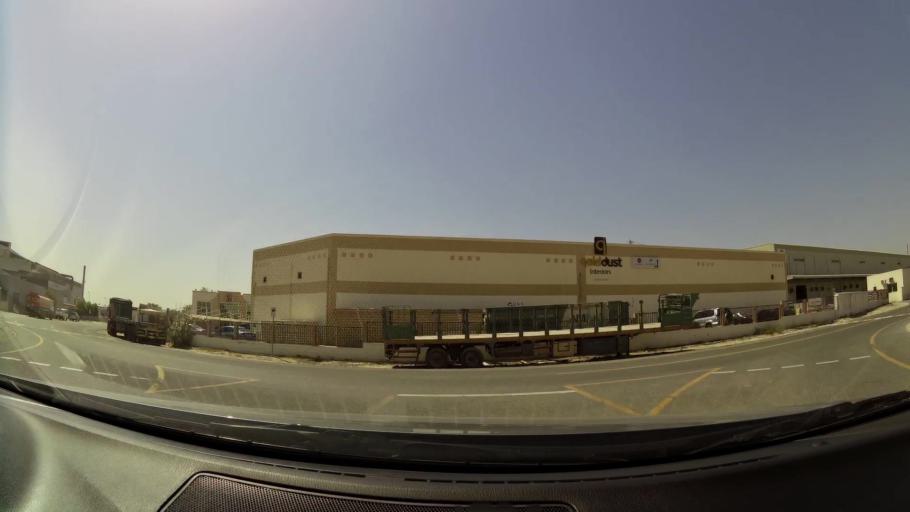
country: AE
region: Dubai
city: Dubai
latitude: 24.9687
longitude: 55.1783
